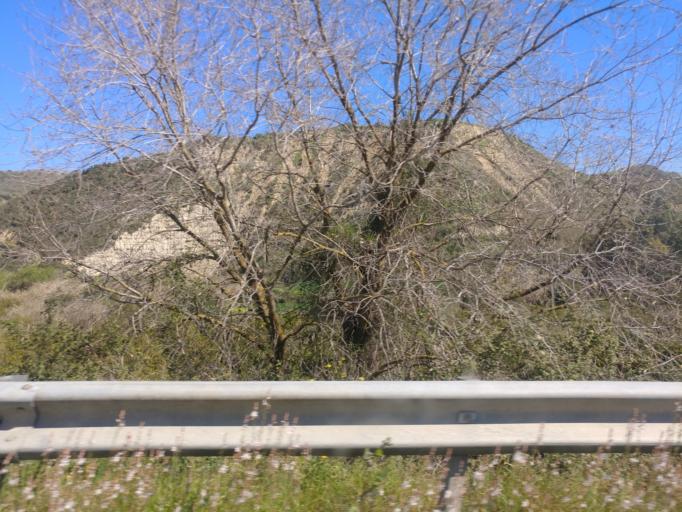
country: CY
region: Pafos
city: Polis
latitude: 34.9623
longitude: 32.4569
